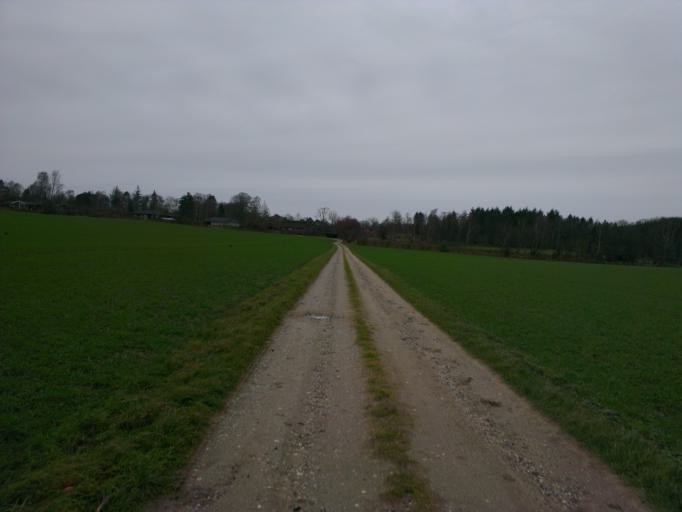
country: DK
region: Capital Region
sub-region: Frederikssund Kommune
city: Jaegerspris
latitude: 55.8468
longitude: 12.0099
